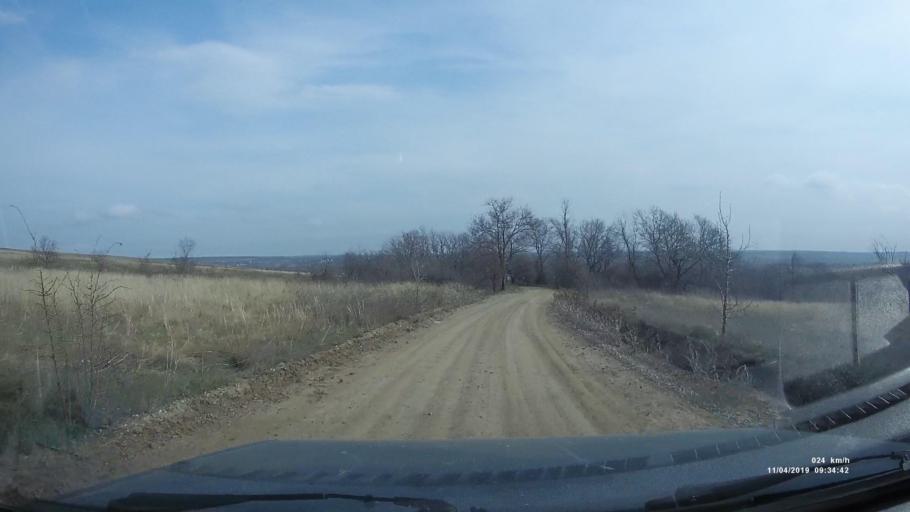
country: RU
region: Rostov
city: Staraya Stanitsa
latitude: 48.2697
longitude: 40.3708
